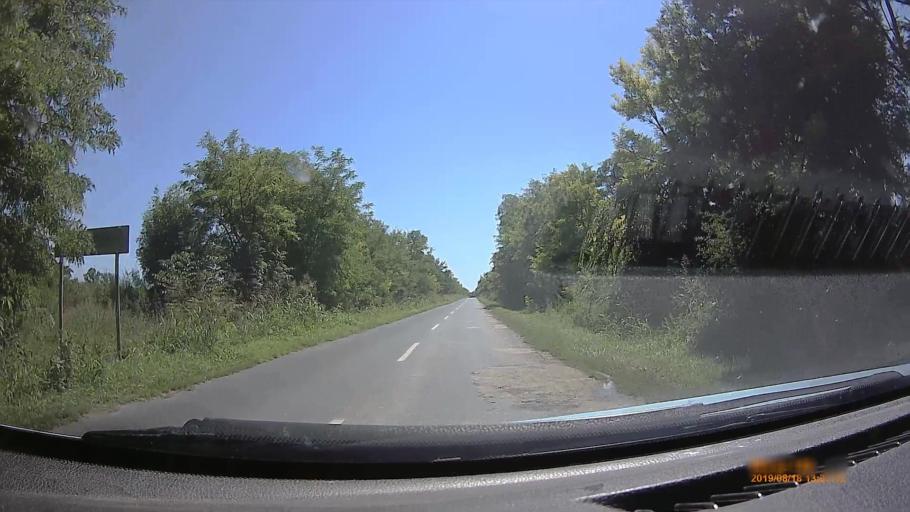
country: HU
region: Fejer
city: Cece
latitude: 46.8071
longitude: 18.5834
